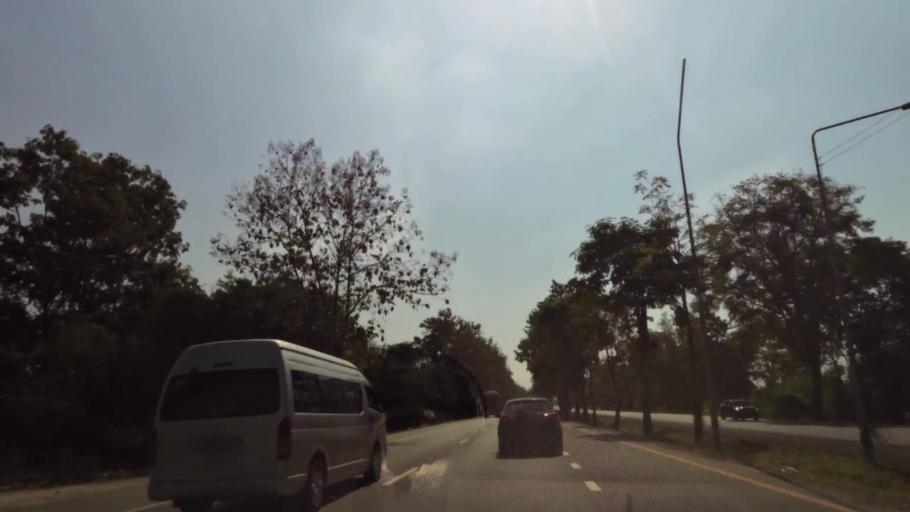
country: TH
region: Phichit
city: Bueng Na Rang
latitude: 16.0624
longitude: 100.1231
